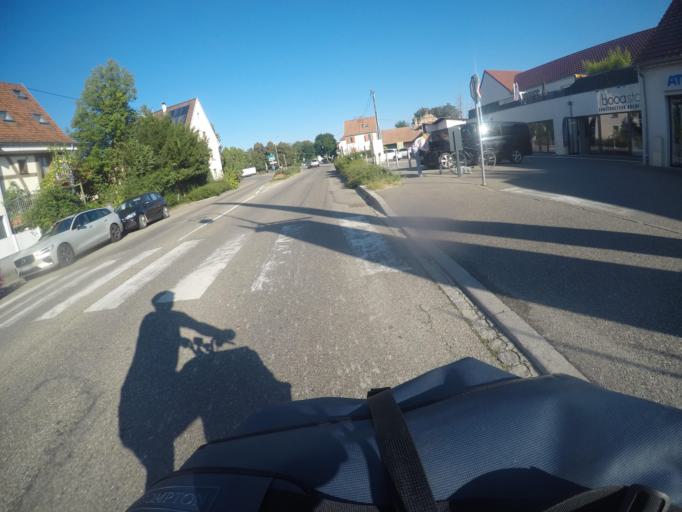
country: FR
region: Alsace
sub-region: Departement du Haut-Rhin
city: Rosenau
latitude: 47.6381
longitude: 7.5142
